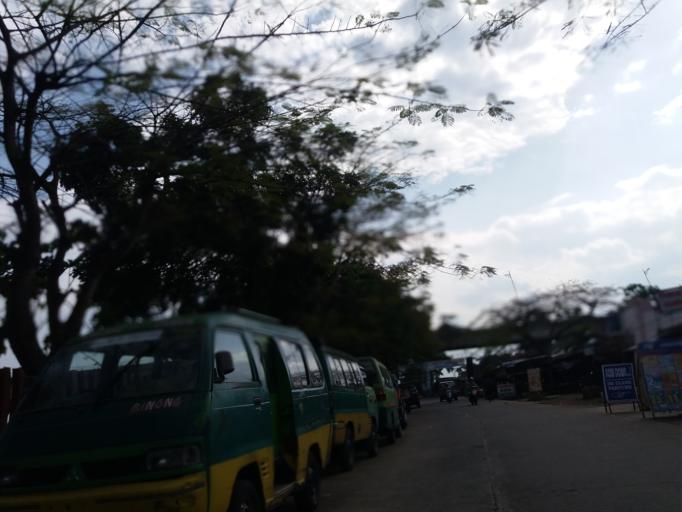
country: ID
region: West Java
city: Bandung
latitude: -6.9238
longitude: 107.6453
